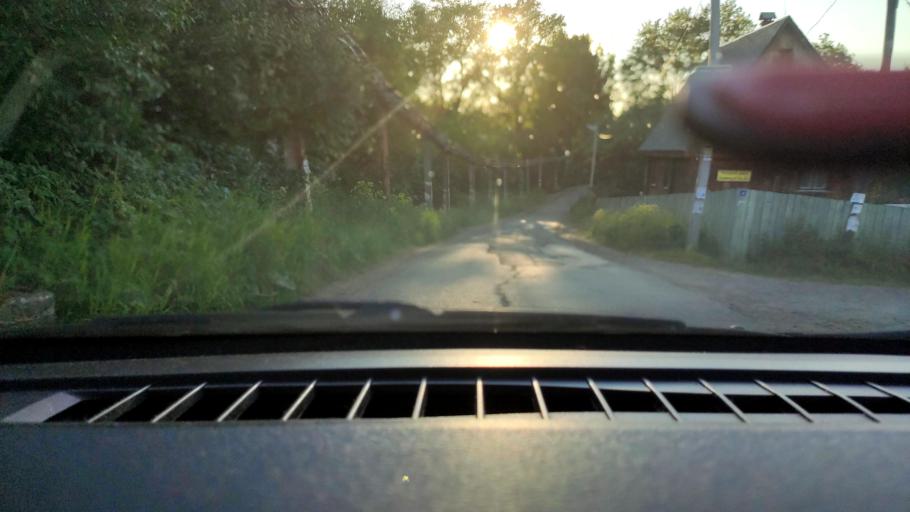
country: RU
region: Perm
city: Kultayevo
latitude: 57.9365
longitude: 55.8627
